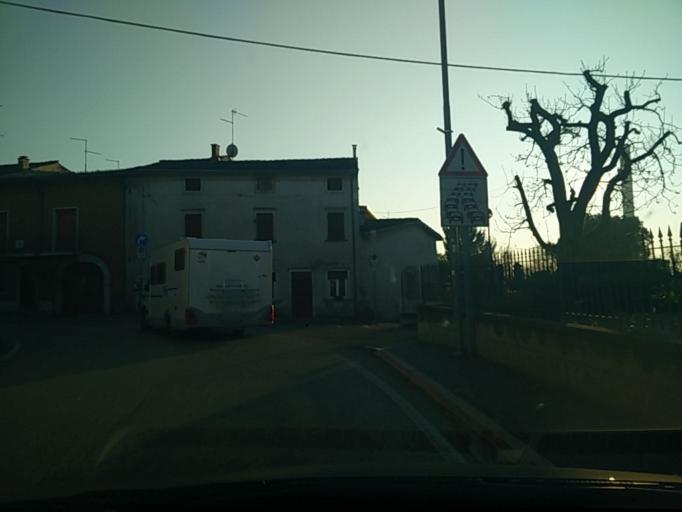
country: IT
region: Veneto
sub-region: Provincia di Verona
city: Salionze
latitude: 45.4033
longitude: 10.7210
